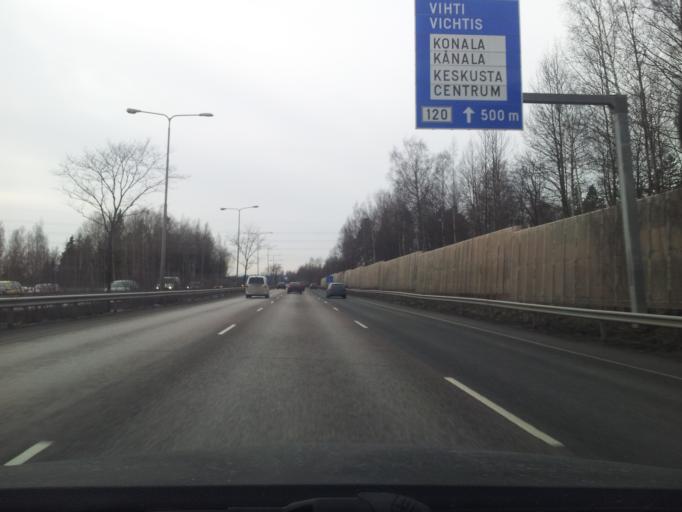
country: FI
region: Uusimaa
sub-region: Helsinki
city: Teekkarikylae
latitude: 60.2347
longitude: 24.8726
